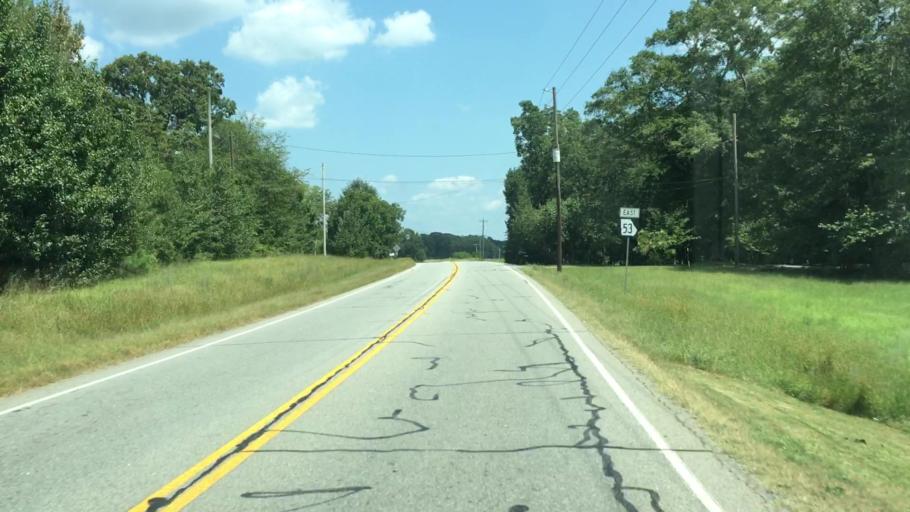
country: US
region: Georgia
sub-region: Oconee County
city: Bogart
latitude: 33.8706
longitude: -83.5051
